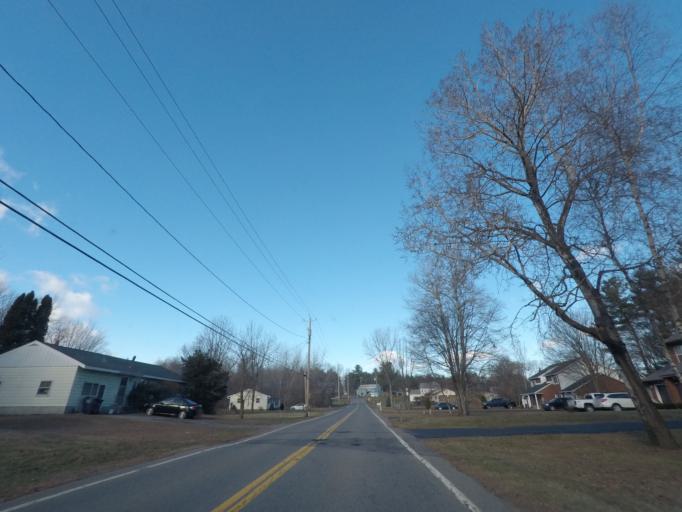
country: US
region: New York
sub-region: Saratoga County
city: Mechanicville
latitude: 42.8736
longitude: -73.7451
